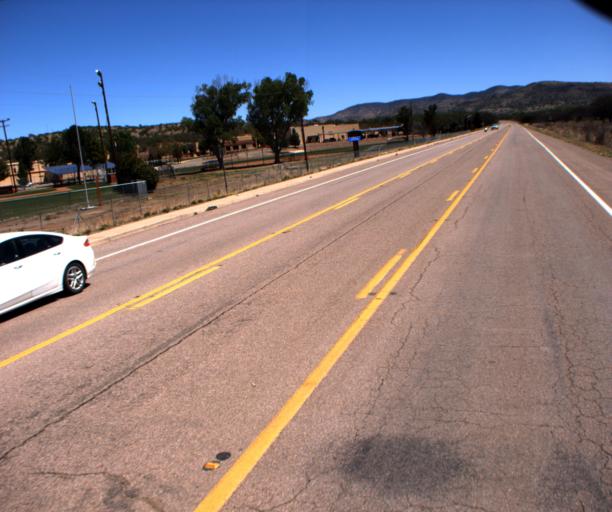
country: US
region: Arizona
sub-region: Santa Cruz County
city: Rio Rico
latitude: 31.5440
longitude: -110.7477
